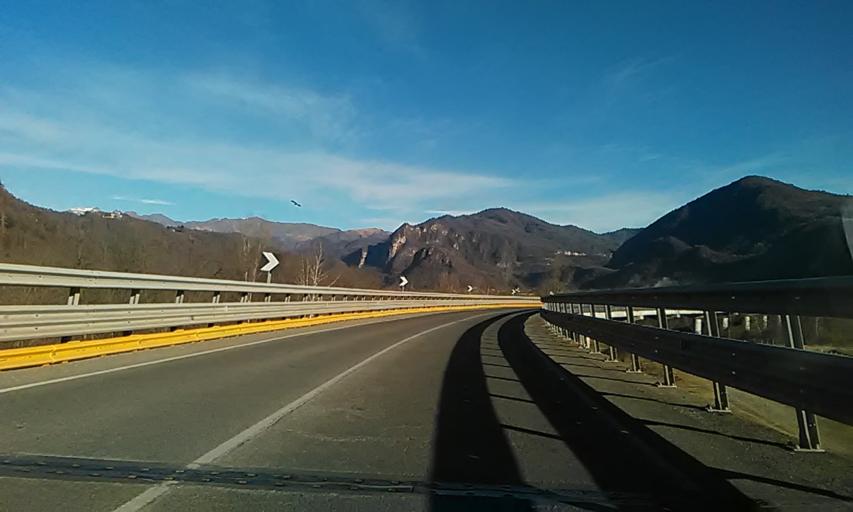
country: IT
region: Piedmont
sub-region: Provincia di Vercelli
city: Quarona
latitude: 45.7687
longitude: 8.2609
